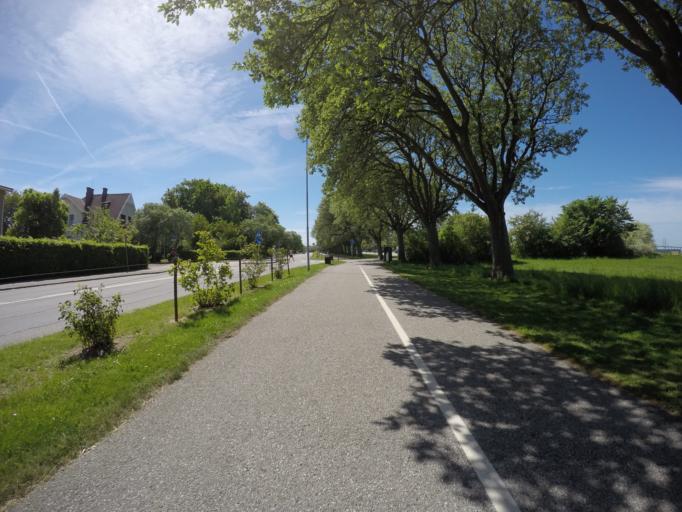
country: SE
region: Skane
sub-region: Malmo
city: Bunkeflostrand
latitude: 55.5776
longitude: 12.9151
